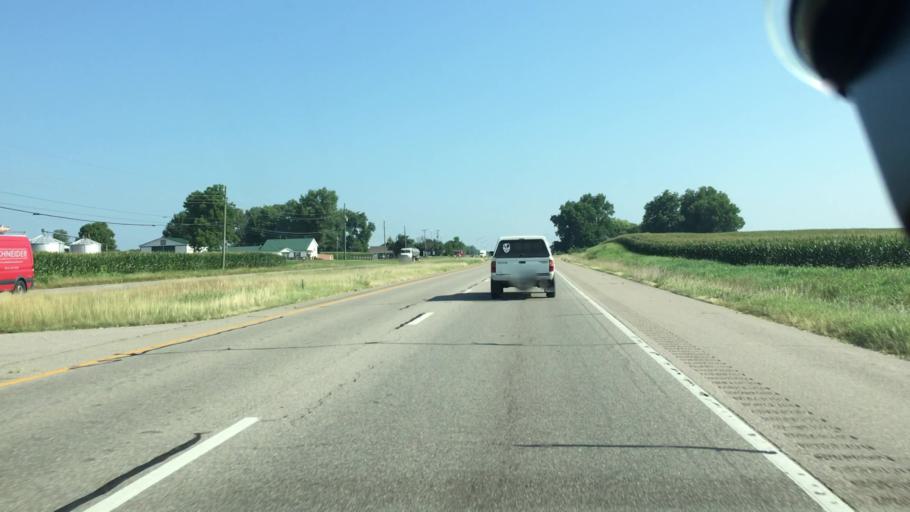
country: US
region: Indiana
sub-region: Gibson County
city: Fort Branch
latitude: 38.2641
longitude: -87.5677
